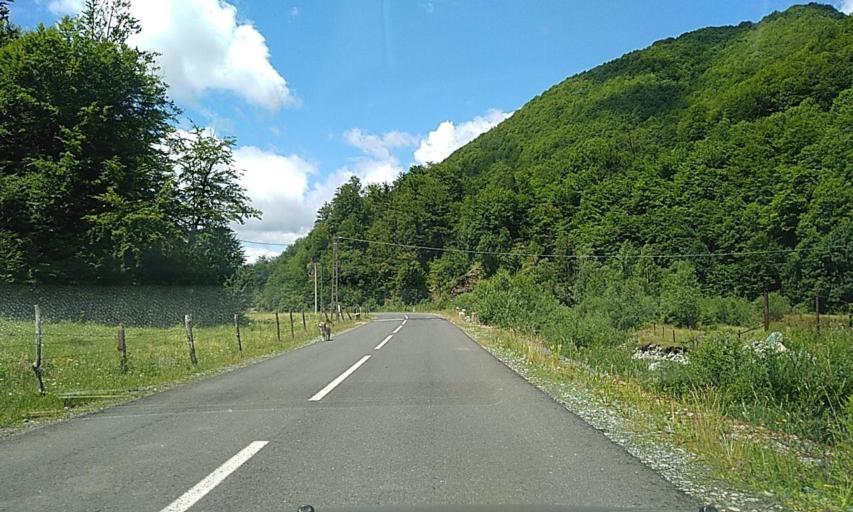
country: RO
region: Hunedoara
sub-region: Oras Petrila
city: Petrila
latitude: 45.4178
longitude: 23.4567
